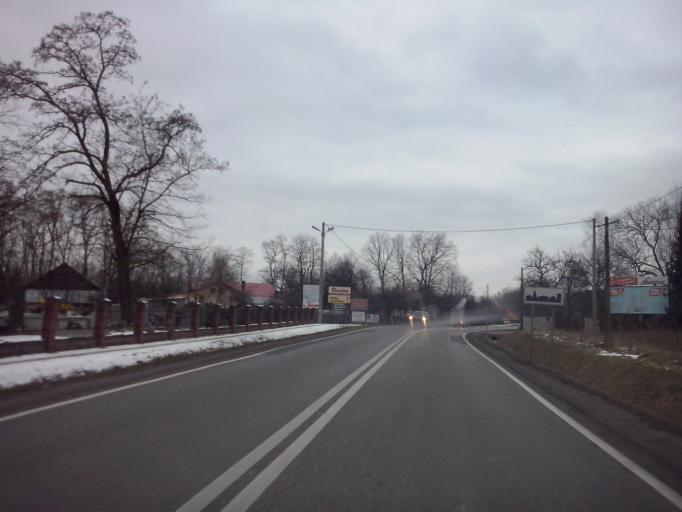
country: PL
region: Subcarpathian Voivodeship
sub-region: Powiat nizanski
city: Raclawice
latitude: 50.5089
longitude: 22.1724
